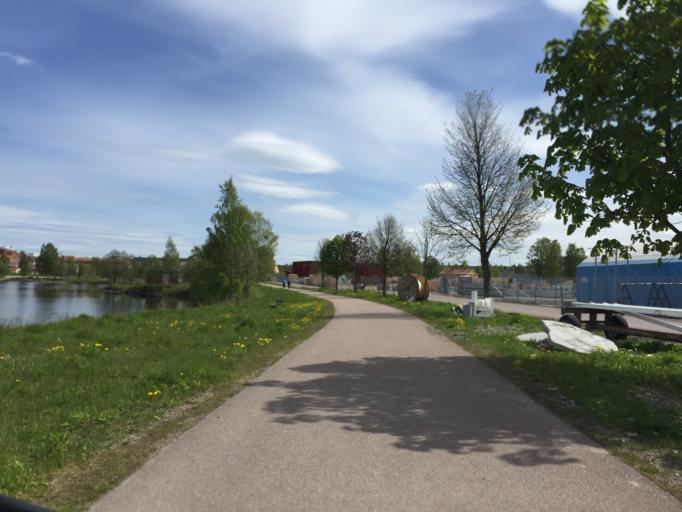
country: SE
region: Dalarna
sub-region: Ludvika Kommun
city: Ludvika
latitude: 60.1483
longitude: 15.1723
